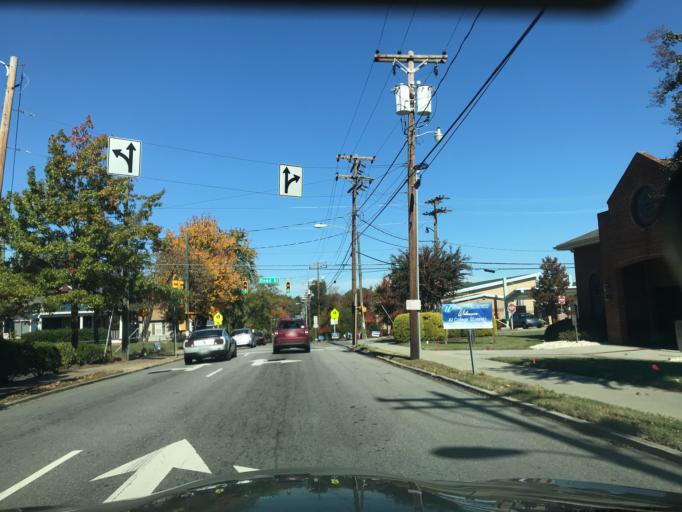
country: US
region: North Carolina
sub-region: Durham County
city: Durham
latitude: 35.9999
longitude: -78.8940
